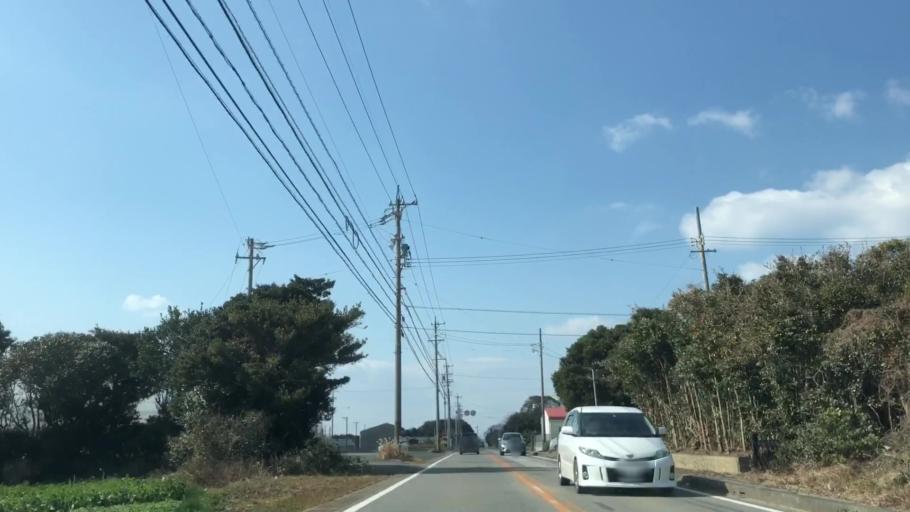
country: JP
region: Aichi
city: Tahara
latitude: 34.5903
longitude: 137.1063
